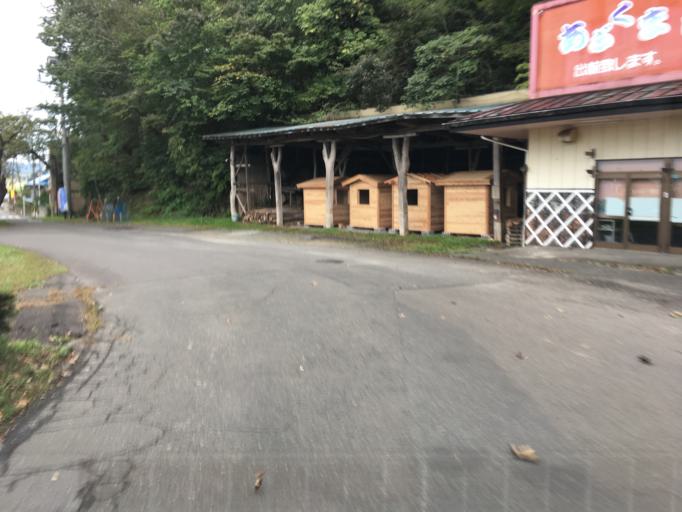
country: JP
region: Miyagi
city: Marumori
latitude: 37.9214
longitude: 140.7608
